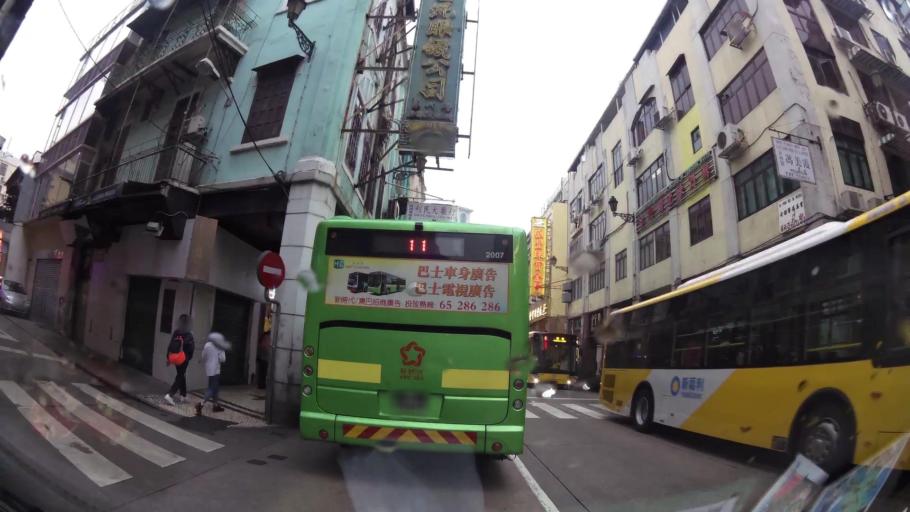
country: MO
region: Macau
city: Macau
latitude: 22.1949
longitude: 113.5380
